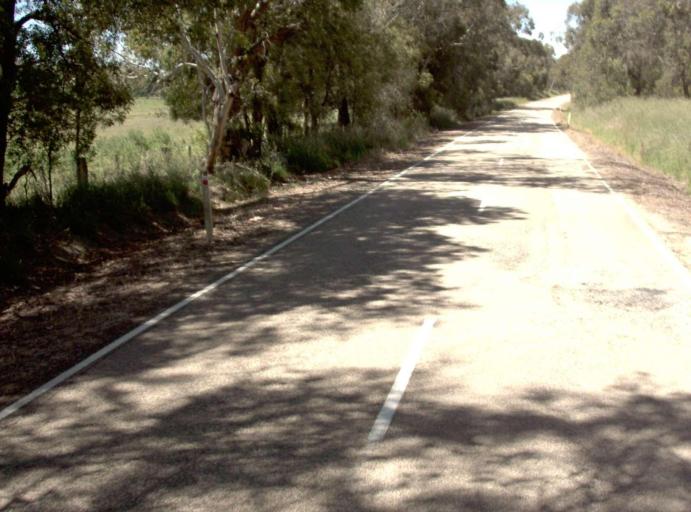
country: AU
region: Victoria
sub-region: East Gippsland
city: Lakes Entrance
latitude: -37.1800
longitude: 148.2691
